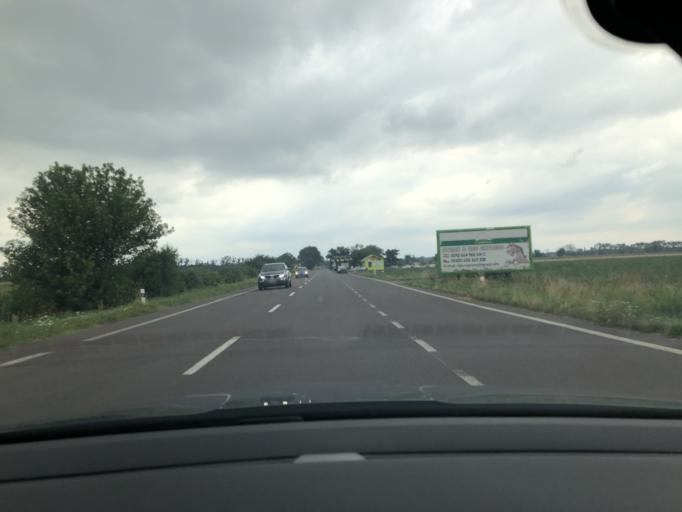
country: CZ
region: South Moravian
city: Hevlin
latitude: 48.7370
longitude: 16.3824
